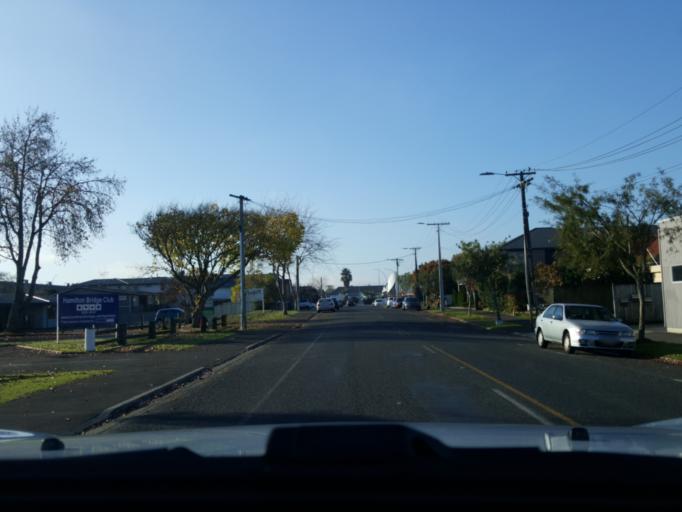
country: NZ
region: Waikato
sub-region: Hamilton City
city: Hamilton
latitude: -37.7784
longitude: 175.2669
